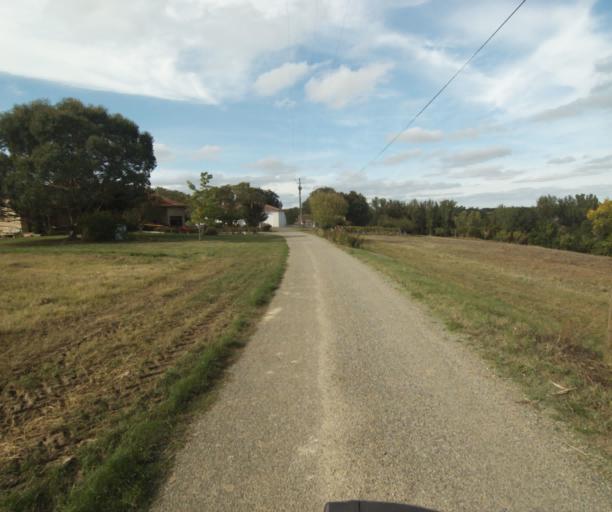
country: FR
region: Midi-Pyrenees
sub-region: Departement du Tarn-et-Garonne
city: Saint-Porquier
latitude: 43.9496
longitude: 1.1324
